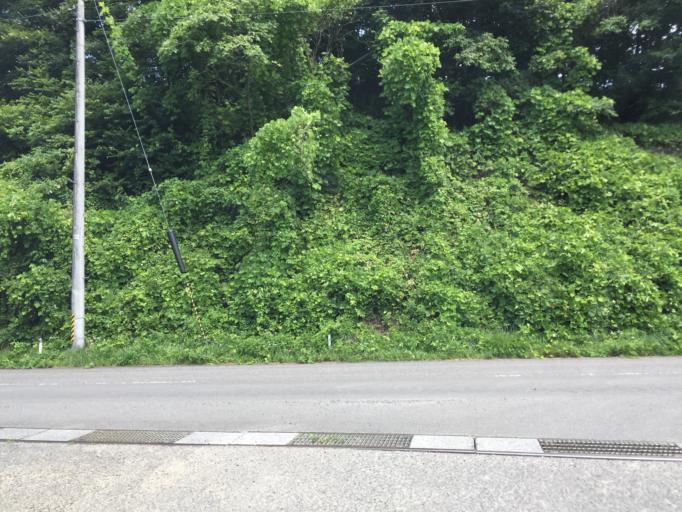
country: JP
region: Fukushima
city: Ishikawa
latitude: 37.2268
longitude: 140.5564
